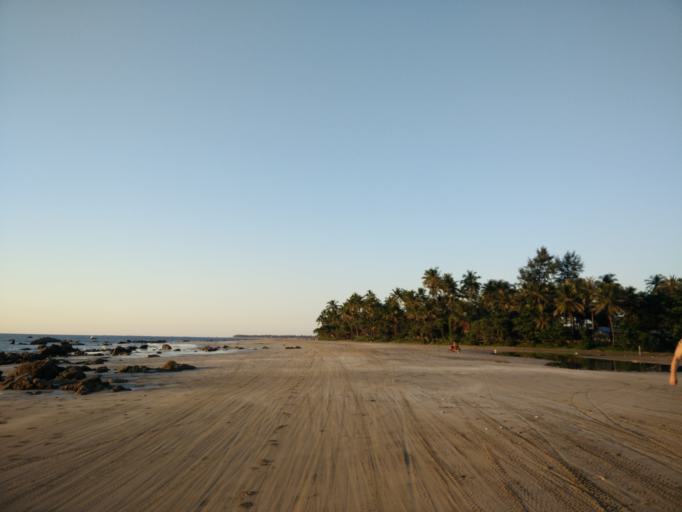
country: MM
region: Ayeyarwady
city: Pathein
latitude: 16.8347
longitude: 94.3927
